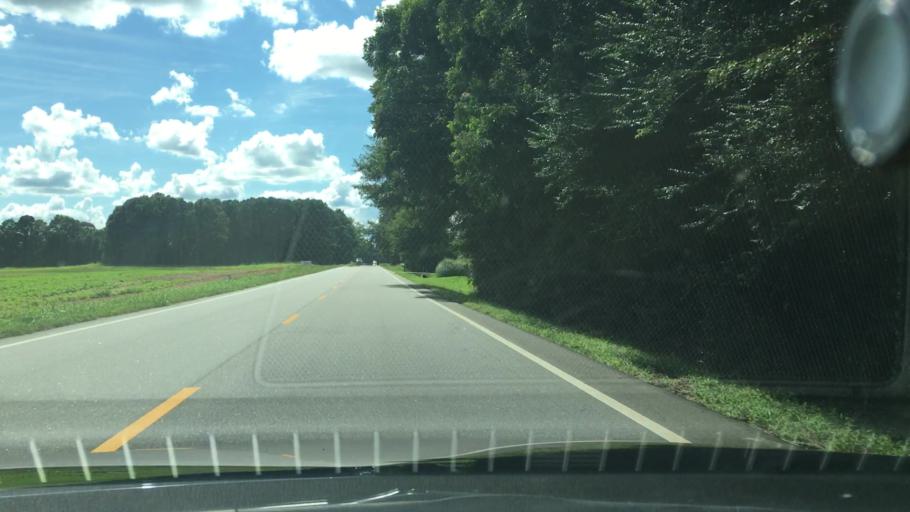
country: US
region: Georgia
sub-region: Butts County
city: Indian Springs
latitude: 33.2883
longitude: -83.9076
